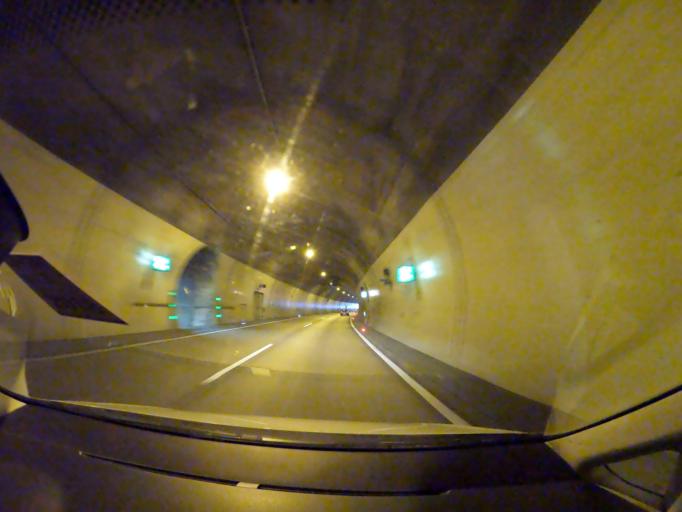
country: AT
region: Styria
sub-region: Politischer Bezirk Voitsberg
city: Modriach
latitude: 46.9771
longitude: 15.0892
